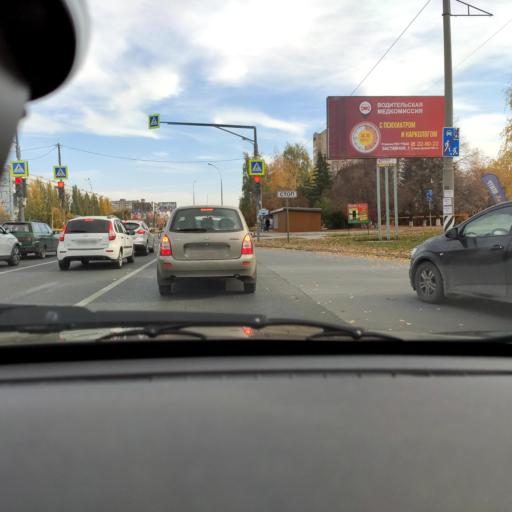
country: RU
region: Samara
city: Tol'yatti
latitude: 53.5263
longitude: 49.3090
